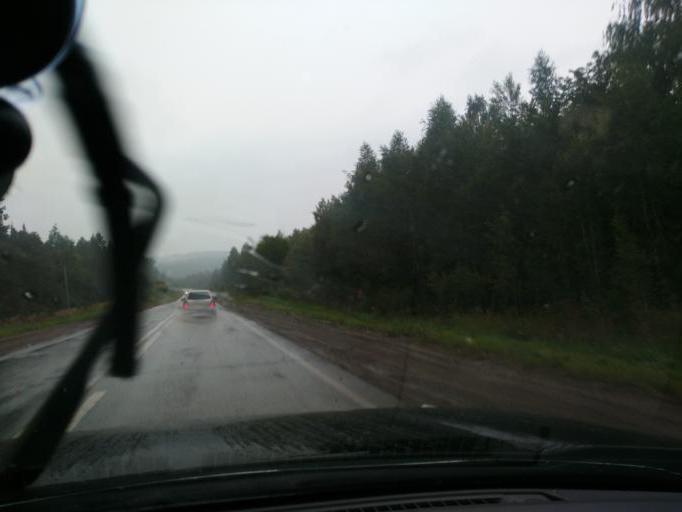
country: RU
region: Perm
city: Barda
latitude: 56.9202
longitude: 55.6804
